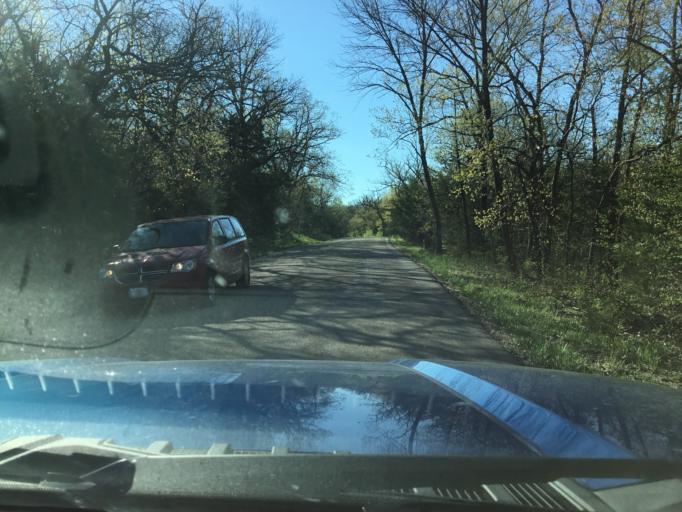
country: US
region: Kansas
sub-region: Douglas County
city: Lawrence
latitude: 38.9899
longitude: -95.2957
